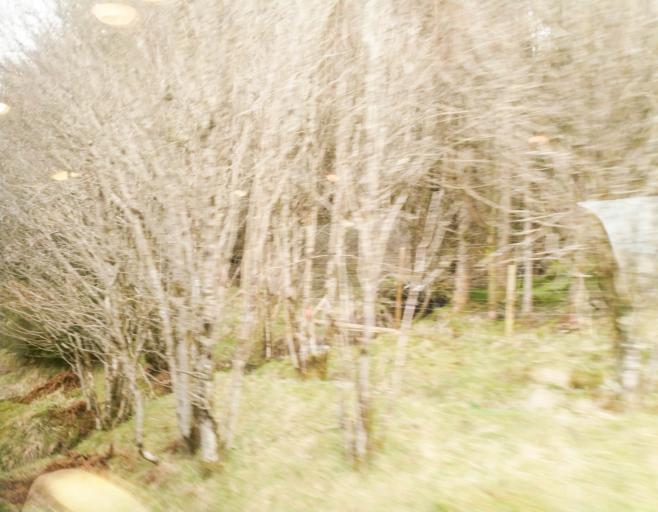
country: GB
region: Scotland
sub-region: Argyll and Bute
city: Garelochhead
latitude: 56.4410
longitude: -4.7074
